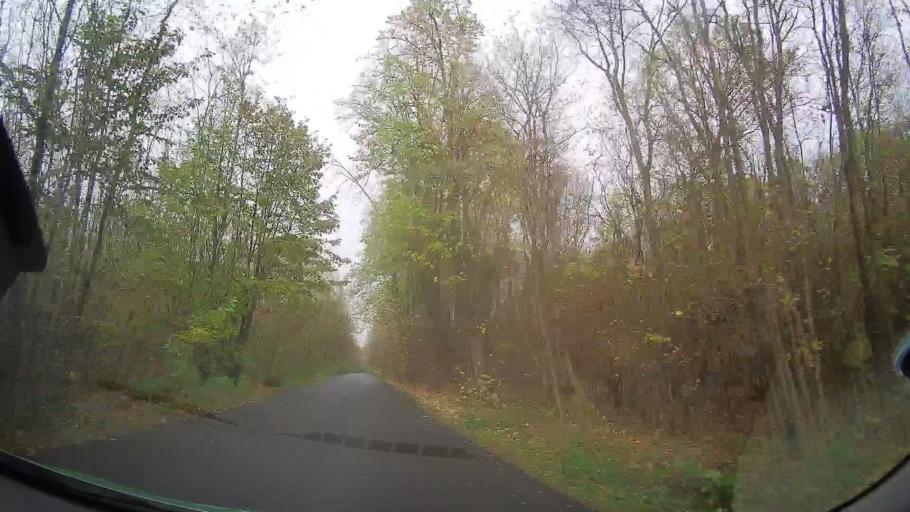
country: RO
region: Prahova
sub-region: Comuna Balta Doamnei
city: Balta Doamnei
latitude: 44.7572
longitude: 26.1301
